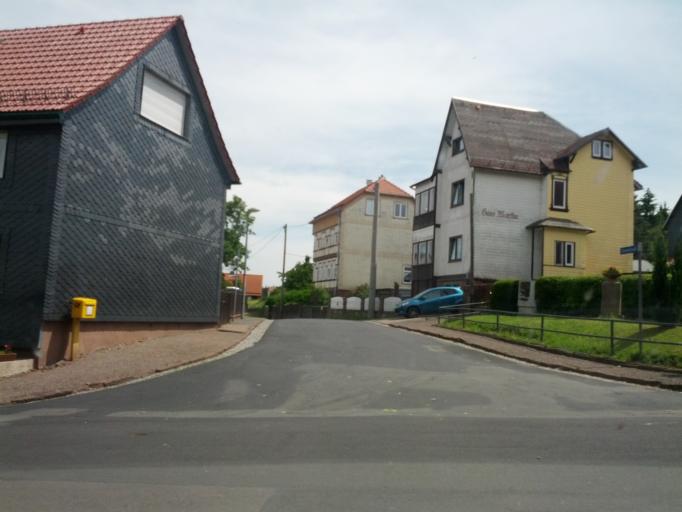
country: DE
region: Thuringia
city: Finsterbergen
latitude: 50.8338
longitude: 10.5835
